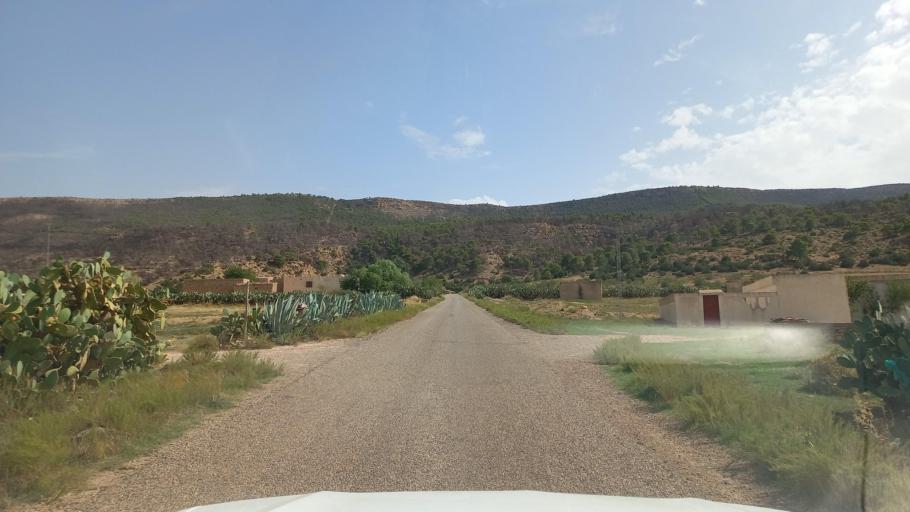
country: TN
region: Al Qasrayn
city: Kasserine
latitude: 35.3555
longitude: 8.8874
